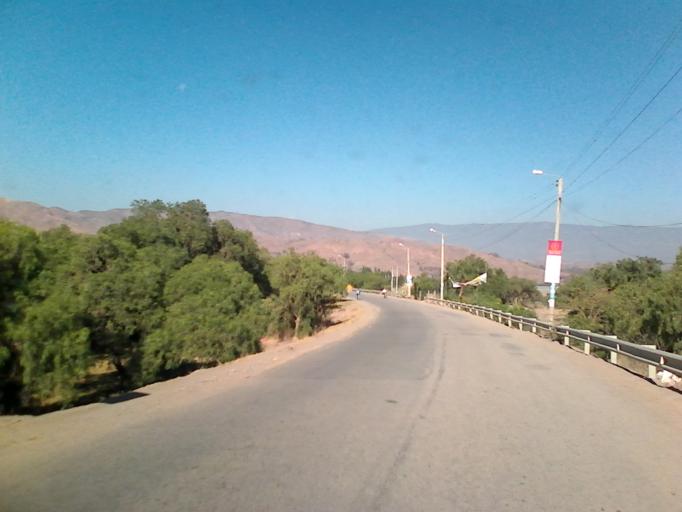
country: CO
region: Boyaca
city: Sachica
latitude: 5.5863
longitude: -73.5333
